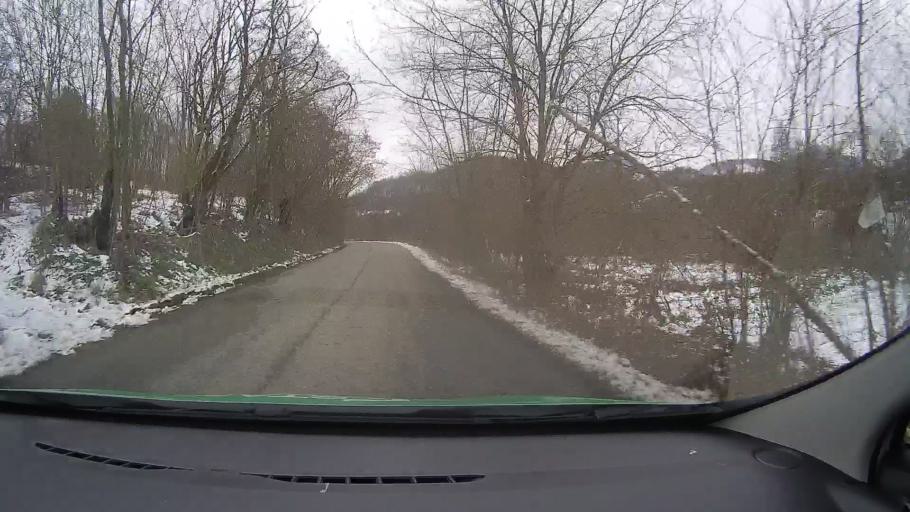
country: RO
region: Hunedoara
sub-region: Comuna Balsa
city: Balsa
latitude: 46.0381
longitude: 23.0758
